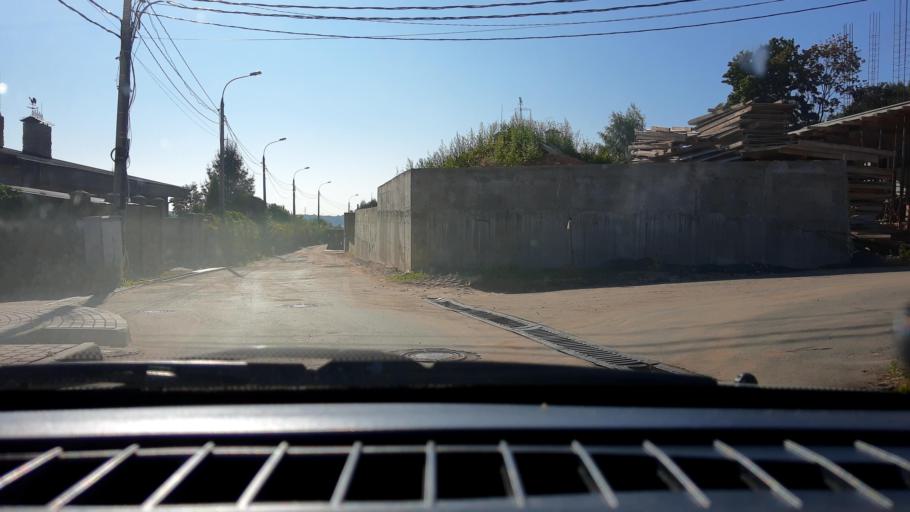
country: RU
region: Nizjnij Novgorod
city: Bor
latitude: 56.3137
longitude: 44.0836
